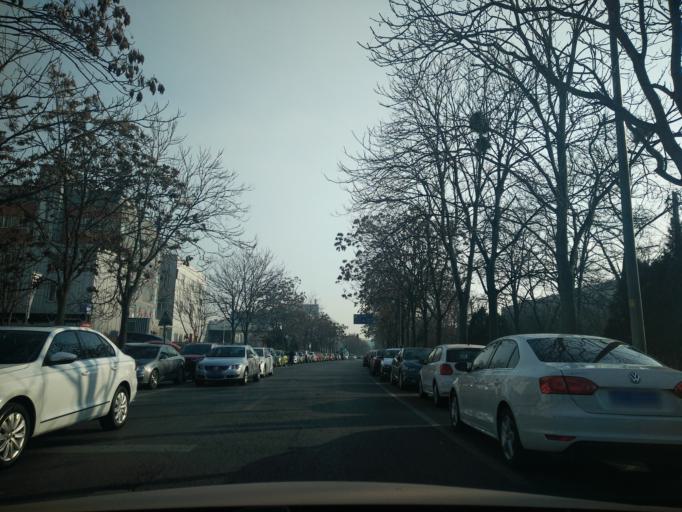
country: CN
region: Beijing
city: Jiugong
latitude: 39.8081
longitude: 116.5063
